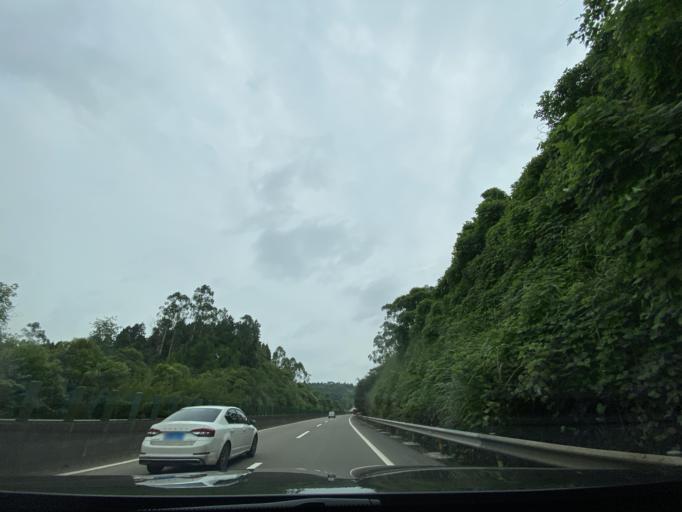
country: CN
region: Sichuan
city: Neijiang
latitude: 29.6583
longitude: 104.9825
